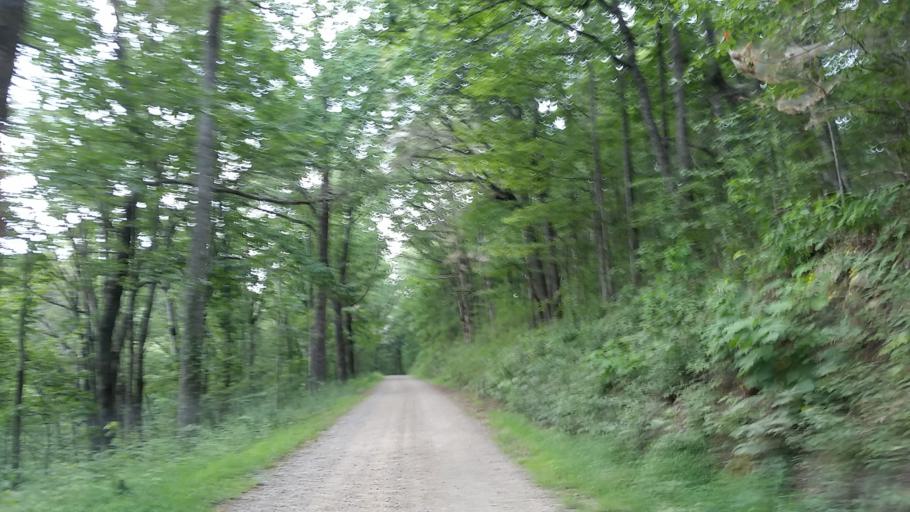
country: US
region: Georgia
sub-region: Lumpkin County
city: Dahlonega
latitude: 34.6471
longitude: -84.0617
